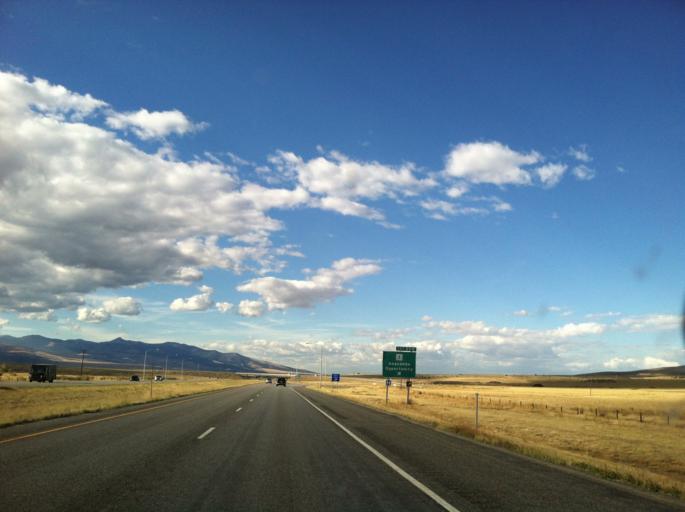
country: US
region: Montana
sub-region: Deer Lodge County
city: Warm Springs
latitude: 46.0878
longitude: -112.7900
